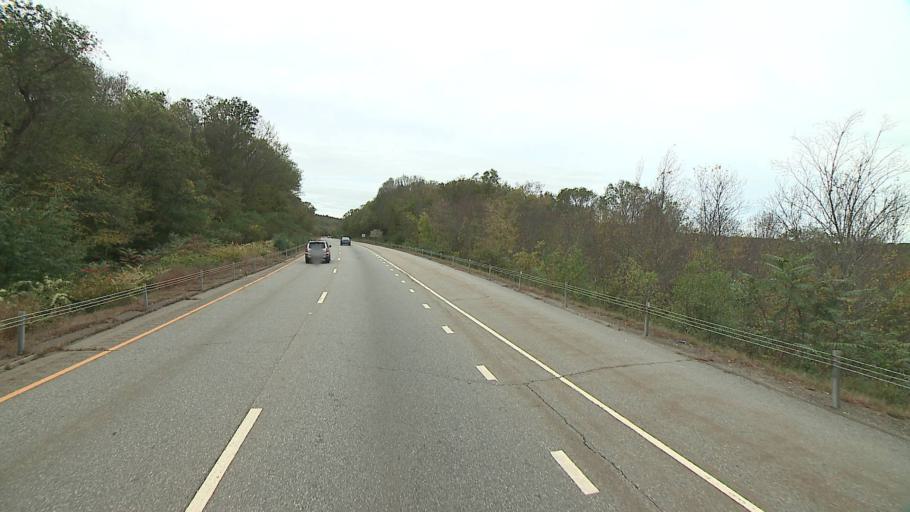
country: US
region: Connecticut
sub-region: Middlesex County
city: Chester Center
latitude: 41.4097
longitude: -72.4785
